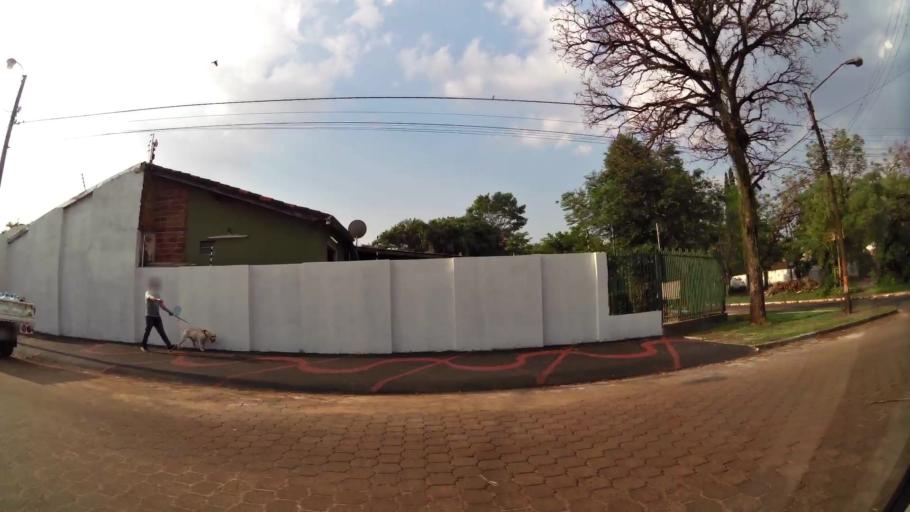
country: PY
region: Alto Parana
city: Presidente Franco
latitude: -25.5214
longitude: -54.6340
